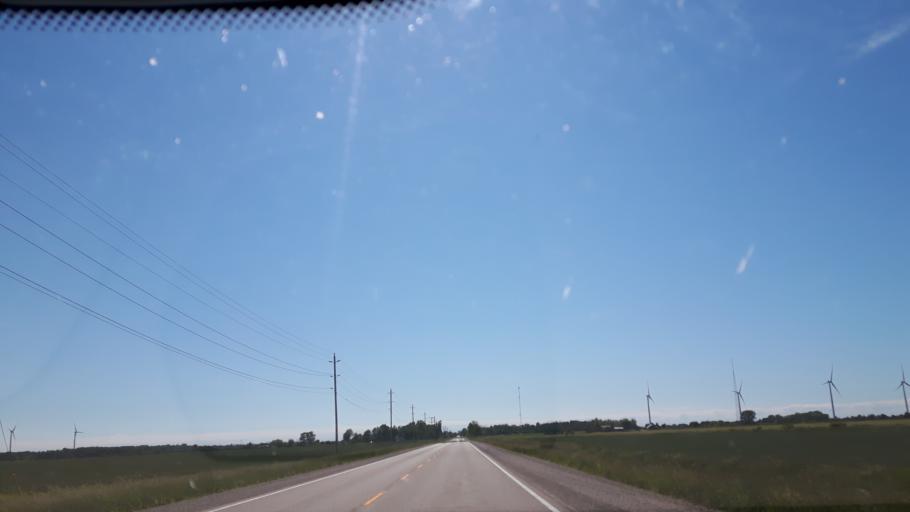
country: CA
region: Ontario
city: Bluewater
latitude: 43.4172
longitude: -81.6633
